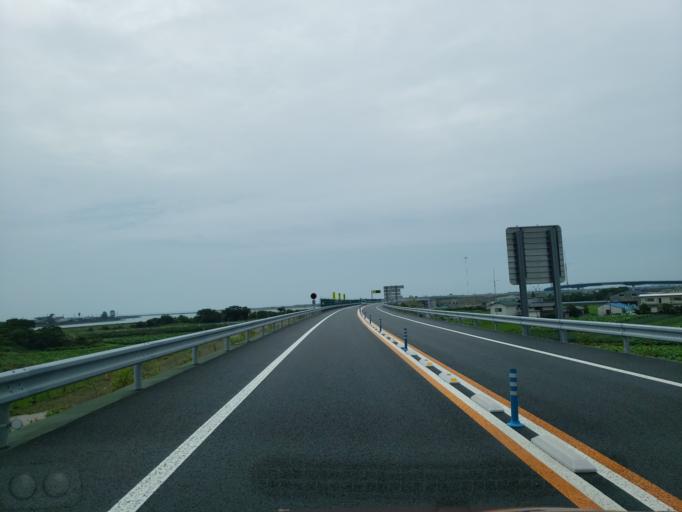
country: JP
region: Tokushima
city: Tokushima-shi
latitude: 34.1117
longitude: 134.5923
